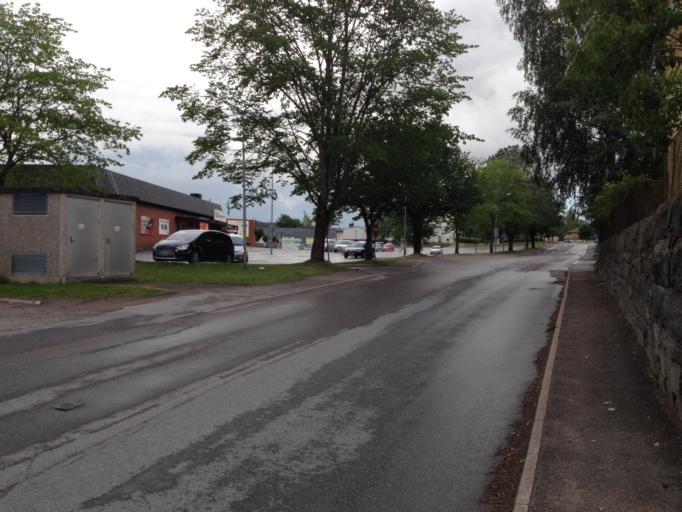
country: SE
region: Vaestra Goetaland
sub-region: Bengtsfors Kommun
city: Bengtsfors
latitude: 59.0297
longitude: 12.2232
